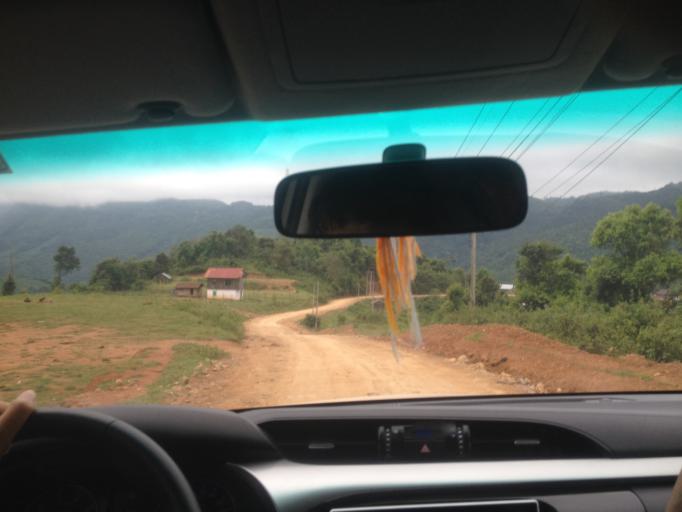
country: TH
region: Nan
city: Chaloem Phra Kiat
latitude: 19.9967
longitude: 101.1313
